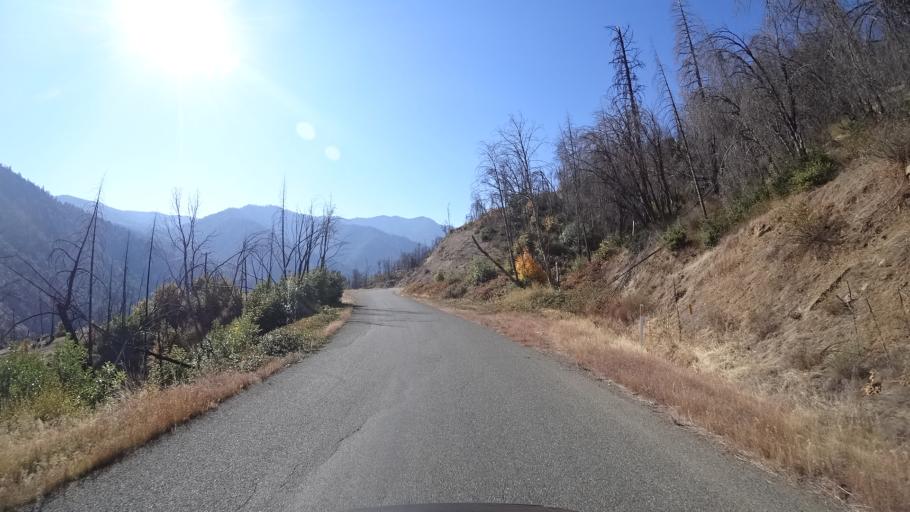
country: US
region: California
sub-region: Siskiyou County
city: Happy Camp
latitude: 41.7234
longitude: -123.0196
